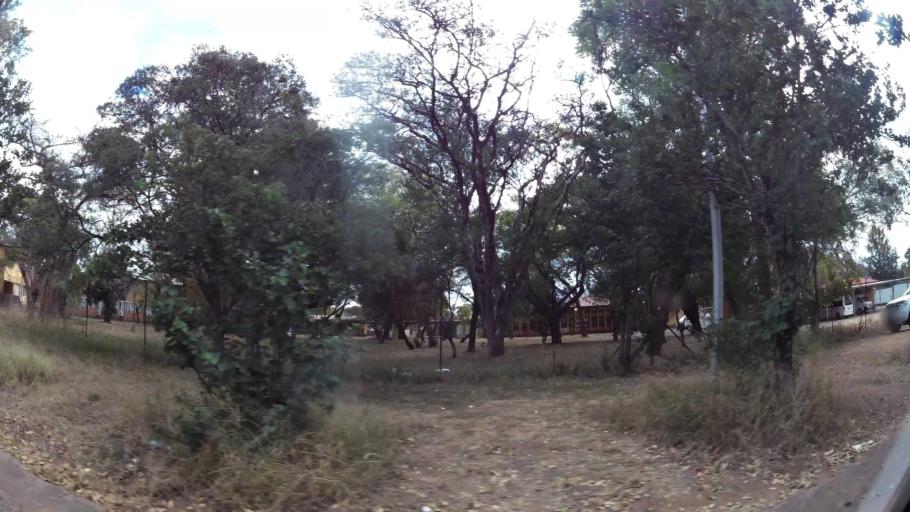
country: ZA
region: Limpopo
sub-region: Waterberg District Municipality
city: Modimolle
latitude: -24.7054
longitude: 28.4024
